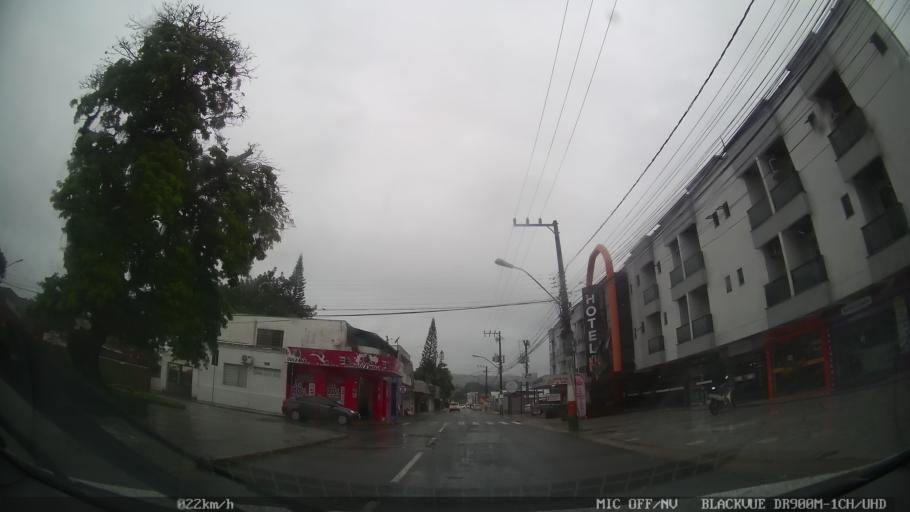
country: BR
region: Santa Catarina
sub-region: Balneario Camboriu
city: Balneario Camboriu
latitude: -27.0235
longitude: -48.6504
